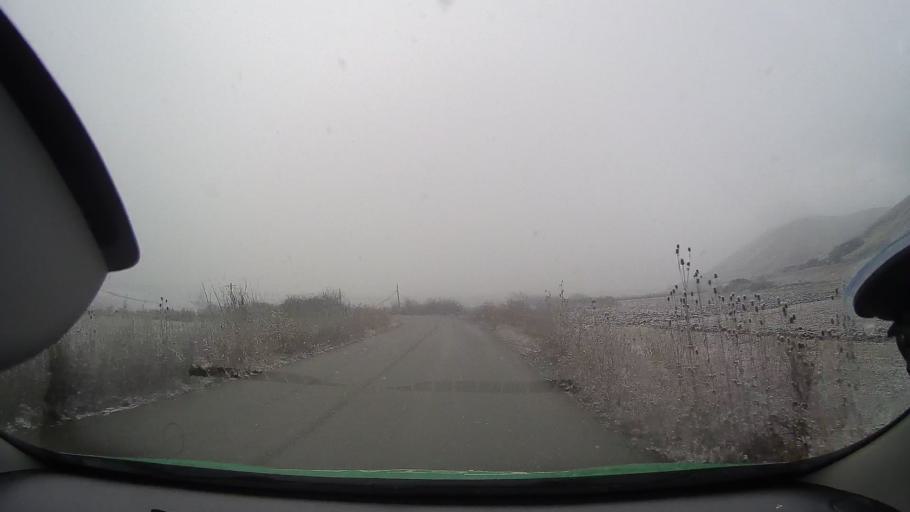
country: RO
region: Alba
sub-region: Comuna Noslac
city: Noslac
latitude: 46.3747
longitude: 23.9164
